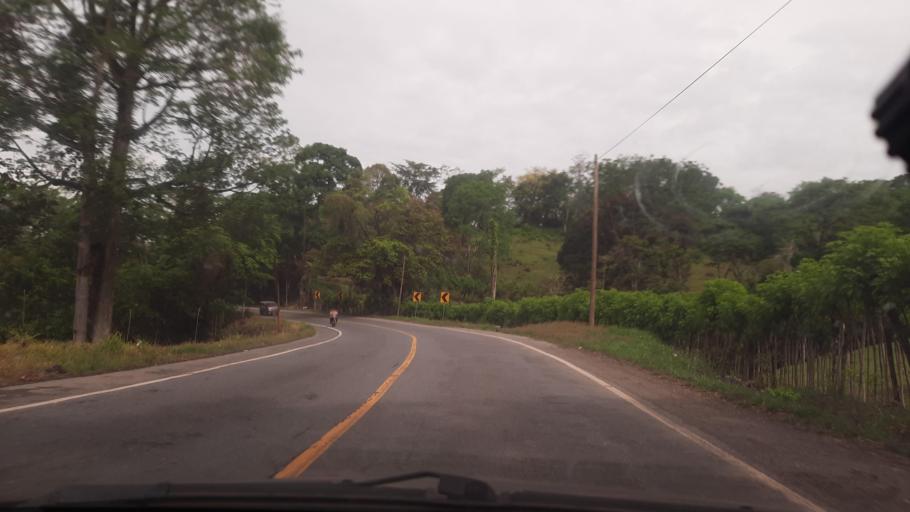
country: GT
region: Izabal
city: Morales
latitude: 15.5225
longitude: -88.7948
